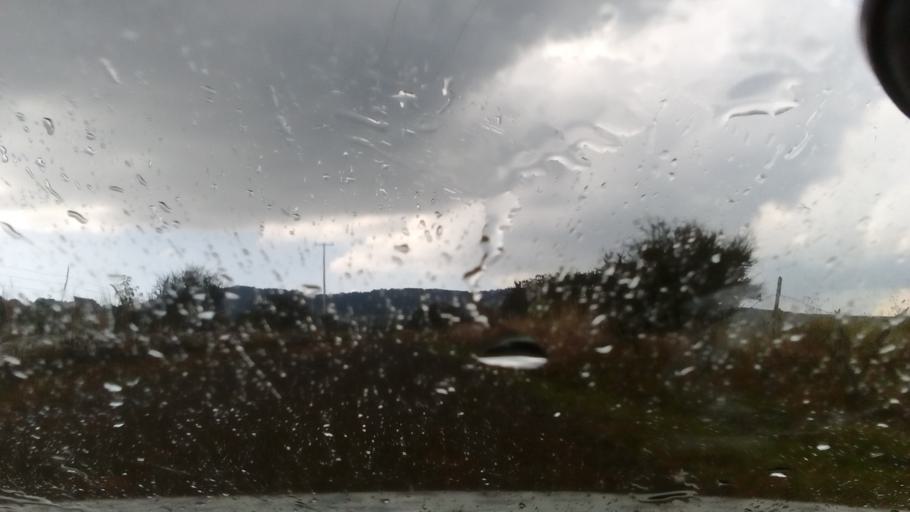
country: MX
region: Guanajuato
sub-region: Silao de la Victoria
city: San Francisco (Banos de Agua Caliente)
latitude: 21.1594
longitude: -101.4205
